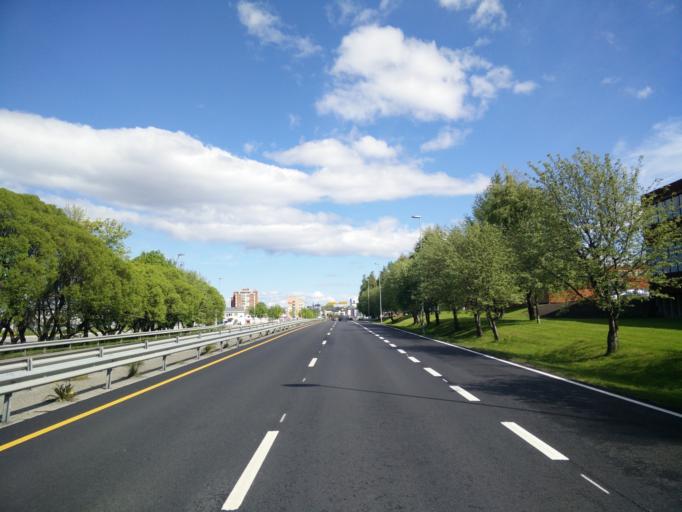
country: NO
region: Sor-Trondelag
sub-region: Trondheim
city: Trondheim
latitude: 63.4023
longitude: 10.3958
